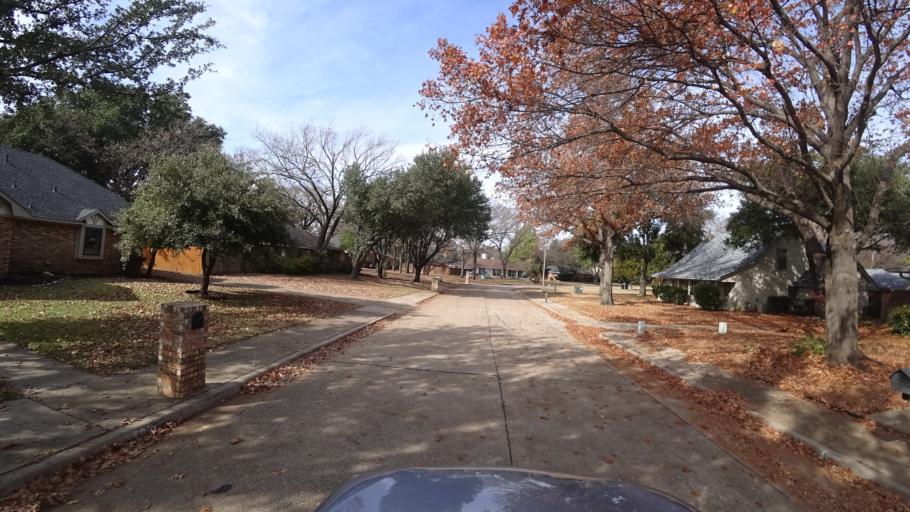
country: US
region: Texas
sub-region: Denton County
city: Highland Village
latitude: 33.0771
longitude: -97.0435
